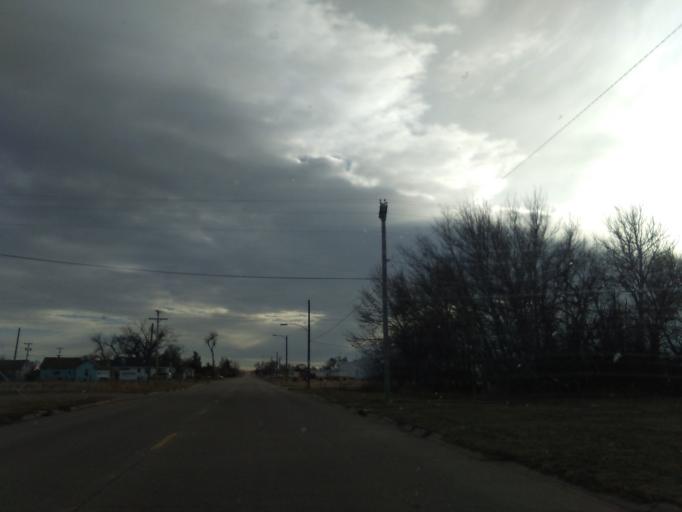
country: US
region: Nebraska
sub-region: Morrill County
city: Bridgeport
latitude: 41.6606
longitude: -103.0996
